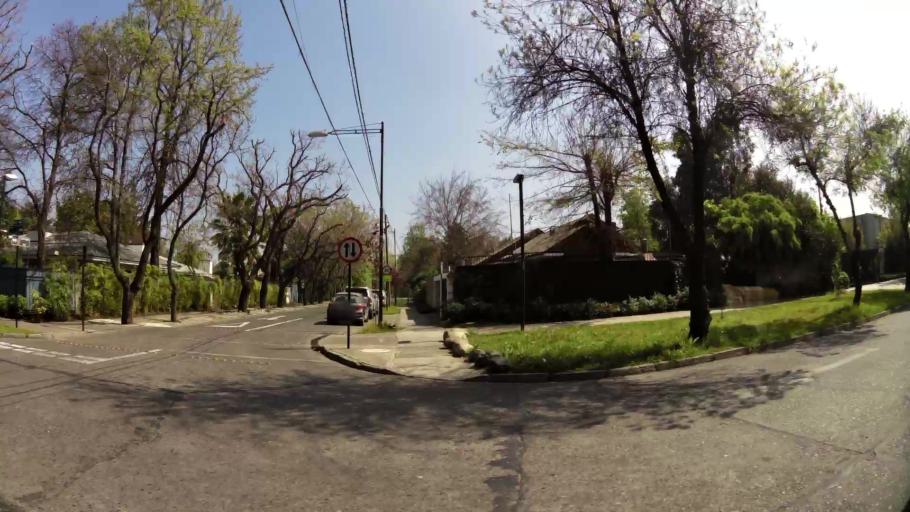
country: CL
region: Santiago Metropolitan
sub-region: Provincia de Santiago
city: Villa Presidente Frei, Nunoa, Santiago, Chile
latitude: -33.3884
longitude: -70.5810
